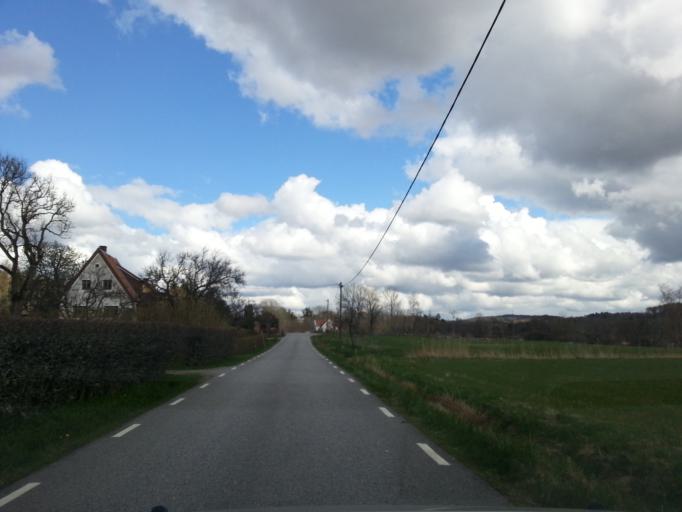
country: SE
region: Vaestra Goetaland
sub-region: Kungalvs Kommun
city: Kungalv
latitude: 57.8539
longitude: 11.9469
